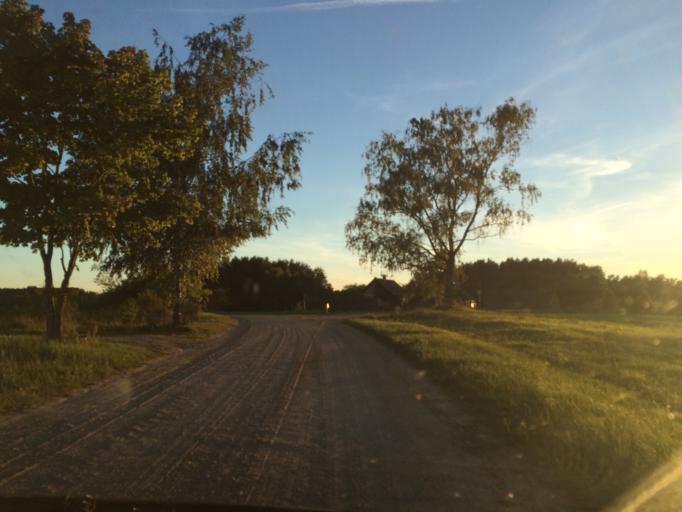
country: LV
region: Aglona
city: Aglona
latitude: 56.2119
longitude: 27.2171
